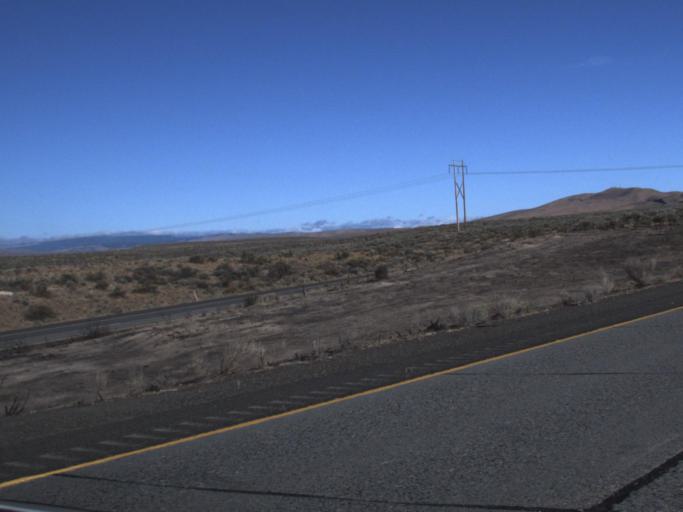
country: US
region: Washington
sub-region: Kittitas County
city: Kittitas
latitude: 46.8288
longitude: -120.3656
